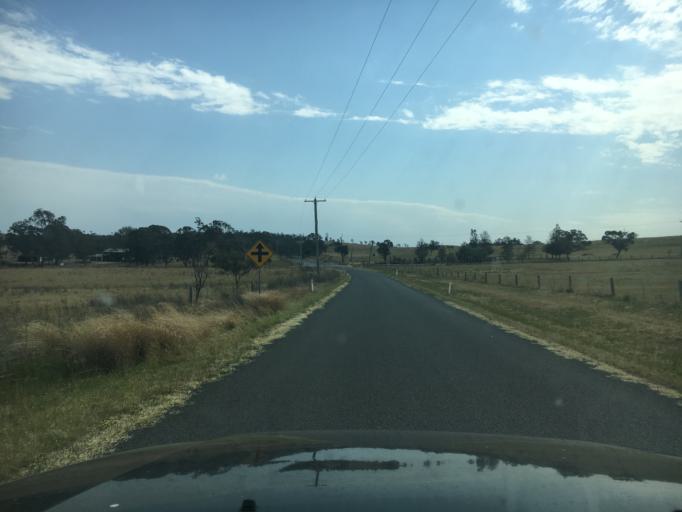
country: AU
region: New South Wales
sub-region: Cessnock
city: Branxton
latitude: -32.5076
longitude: 151.3178
